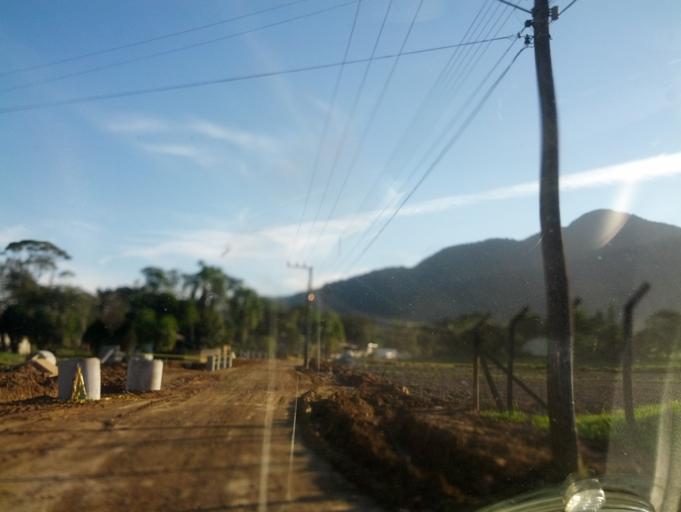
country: BR
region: Santa Catarina
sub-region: Indaial
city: Indaial
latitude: -26.9093
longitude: -49.2661
